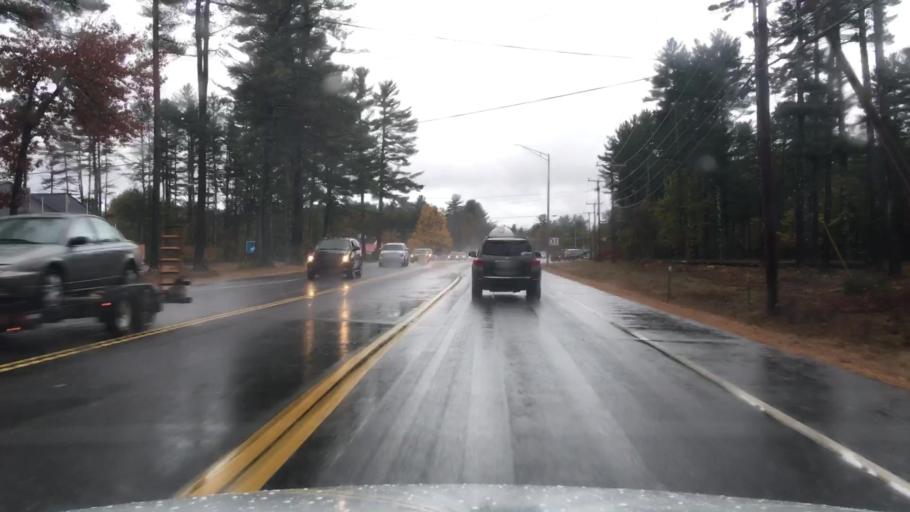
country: US
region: New Hampshire
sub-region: Strafford County
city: Barrington
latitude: 43.2154
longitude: -70.9946
